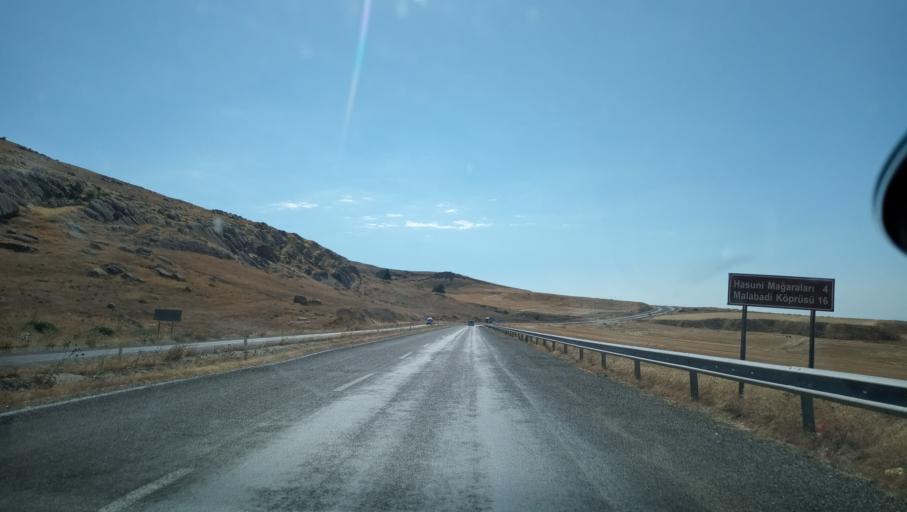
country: TR
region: Diyarbakir
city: Silvan
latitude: 38.1328
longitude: 41.0453
